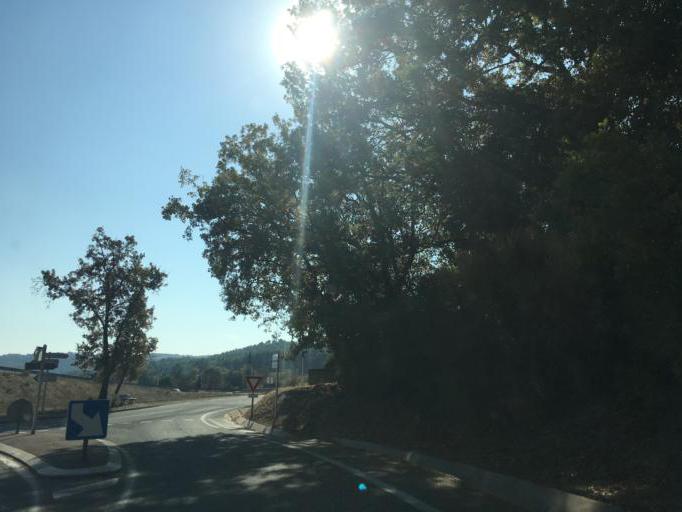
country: FR
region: Provence-Alpes-Cote d'Azur
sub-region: Departement du Var
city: Figanieres
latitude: 43.5705
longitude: 6.5066
